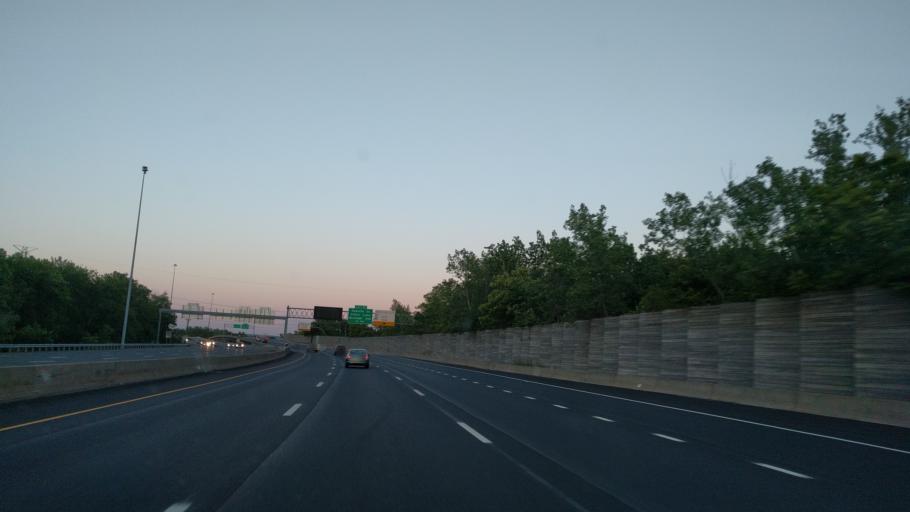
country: US
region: Connecticut
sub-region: Hartford County
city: East Hartford
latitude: 41.7636
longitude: -72.6427
